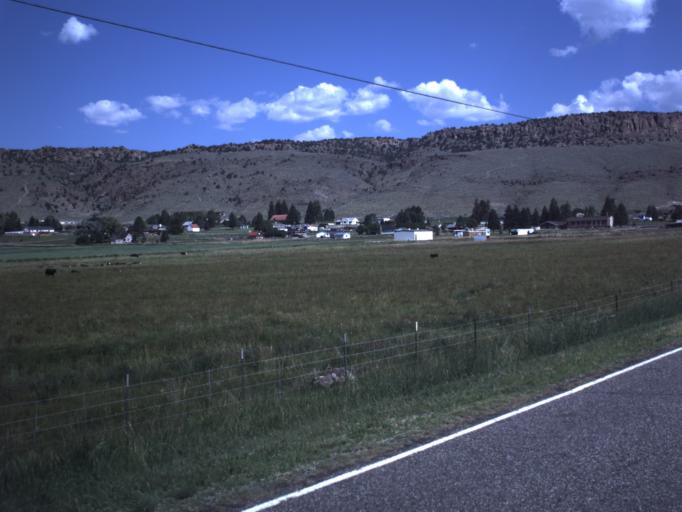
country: US
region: Utah
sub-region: Wayne County
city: Loa
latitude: 38.4518
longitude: -111.6158
